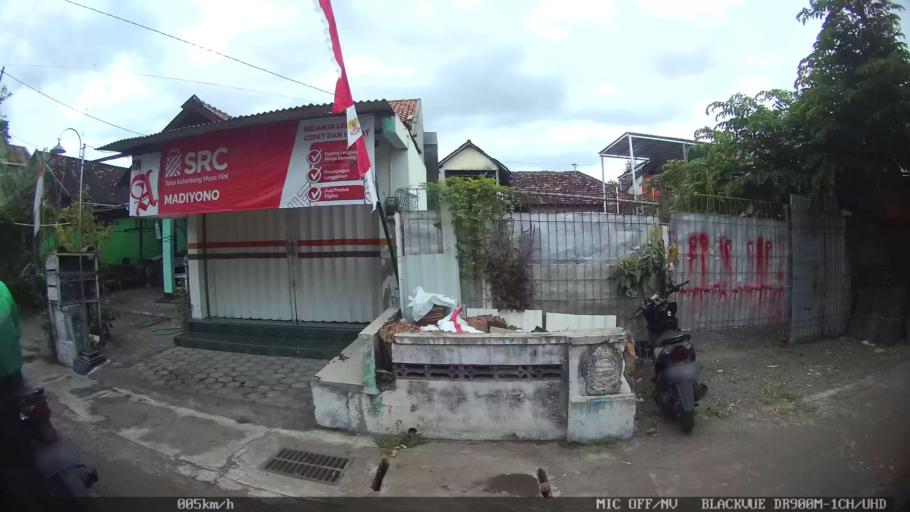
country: ID
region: Daerah Istimewa Yogyakarta
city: Depok
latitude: -7.8054
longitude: 110.4158
